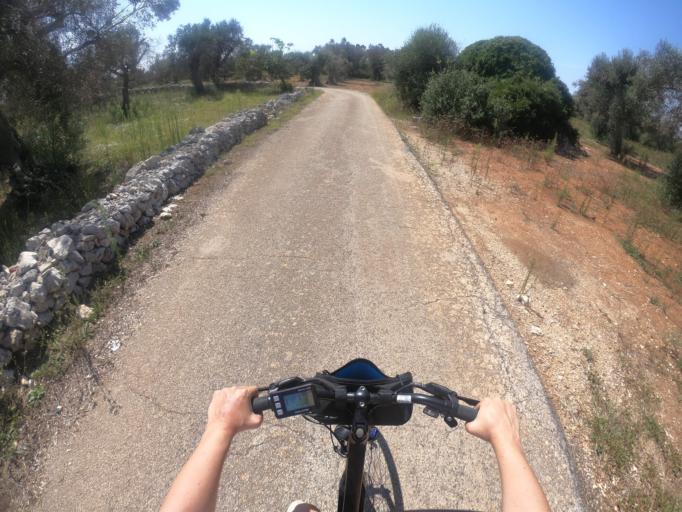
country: IT
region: Apulia
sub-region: Provincia di Lecce
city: Specchia
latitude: 39.9315
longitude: 18.2757
